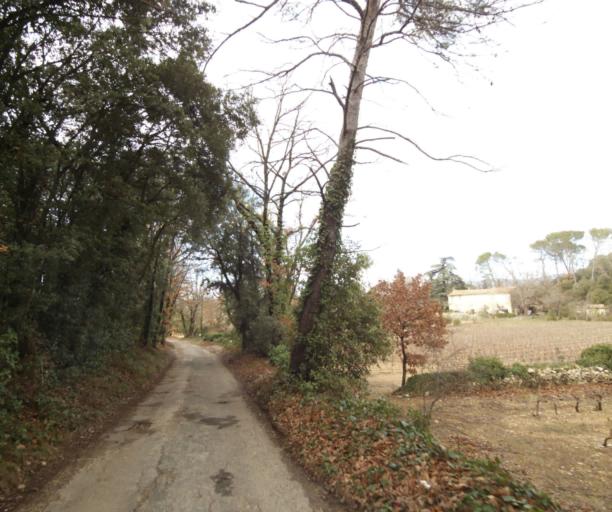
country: FR
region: Provence-Alpes-Cote d'Azur
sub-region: Departement du Var
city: Trans-en-Provence
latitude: 43.5180
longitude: 6.4903
